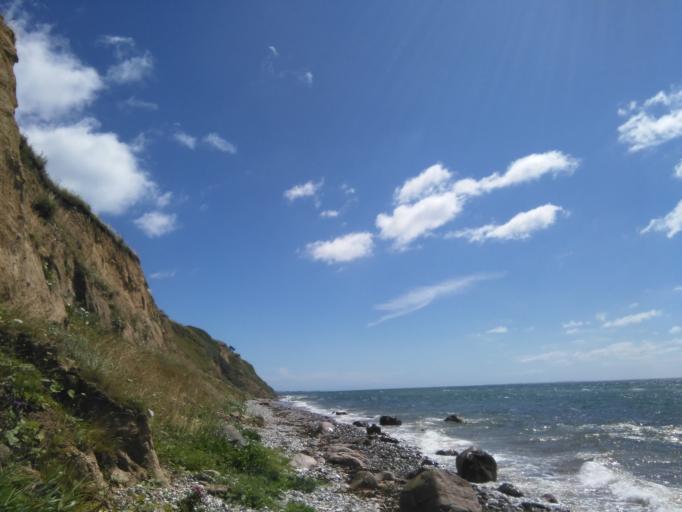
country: DK
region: Central Jutland
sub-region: Arhus Kommune
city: Logten
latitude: 56.1668
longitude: 10.3811
